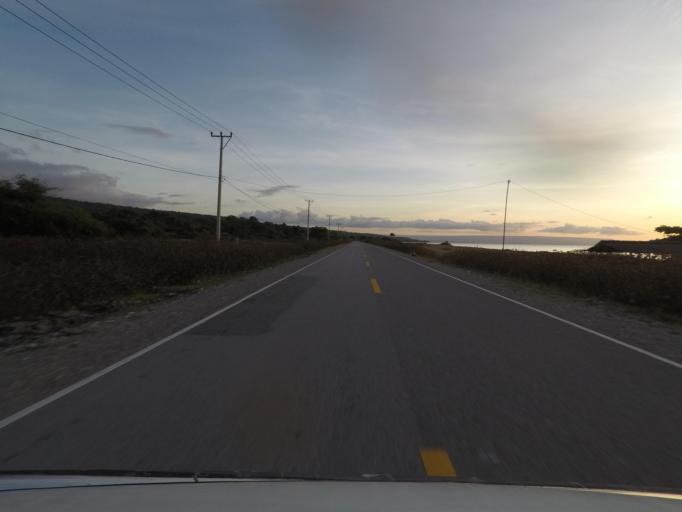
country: TL
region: Baucau
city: Baucau
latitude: -8.4447
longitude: 126.6489
